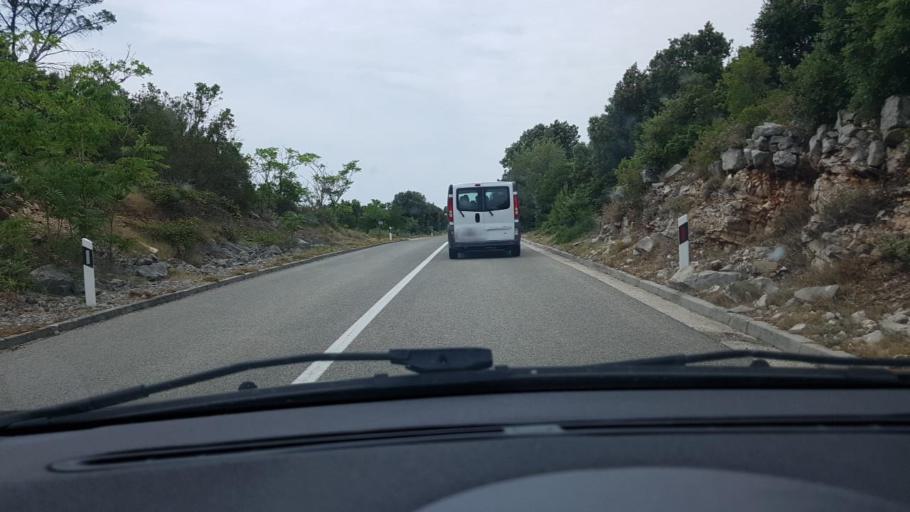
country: HR
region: Dubrovacko-Neretvanska
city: Smokvica
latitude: 42.9489
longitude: 16.9834
